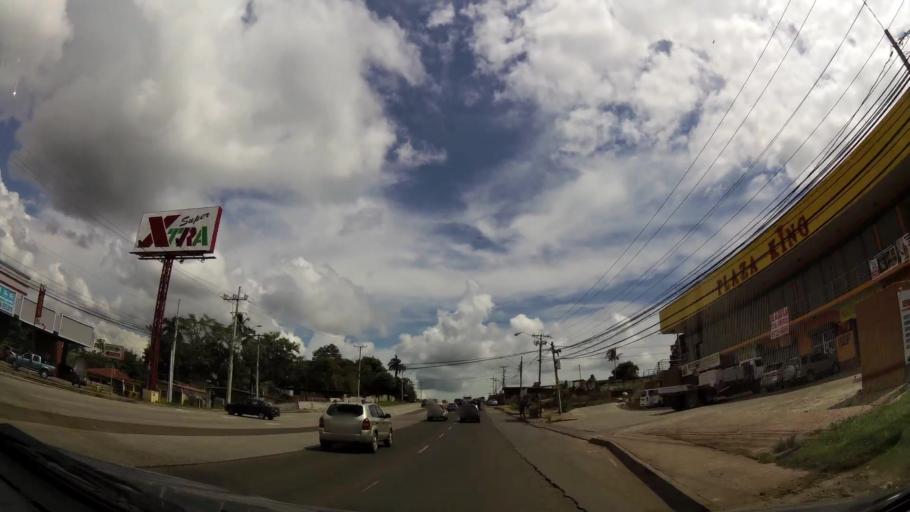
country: PA
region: Panama
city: Vista Alegre
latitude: 8.9309
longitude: -79.7010
